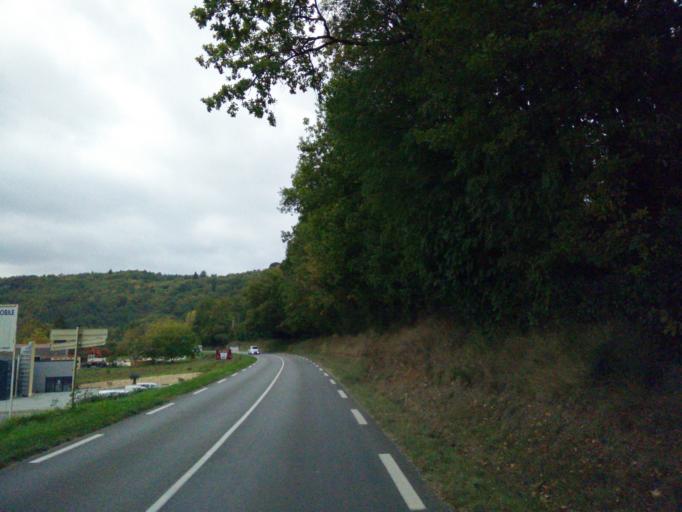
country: FR
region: Midi-Pyrenees
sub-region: Departement du Lot
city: Prayssac
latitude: 44.5067
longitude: 1.1727
